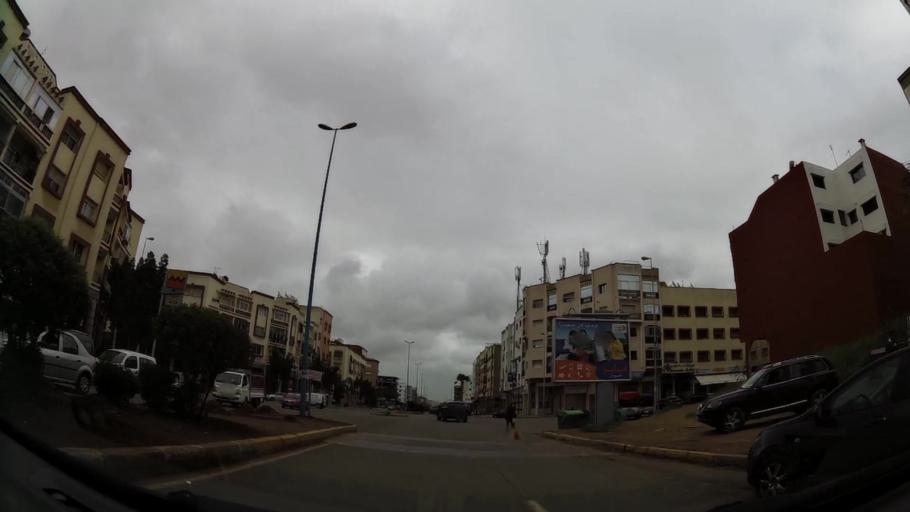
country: MA
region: Grand Casablanca
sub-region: Casablanca
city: Casablanca
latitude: 33.5330
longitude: -7.6145
